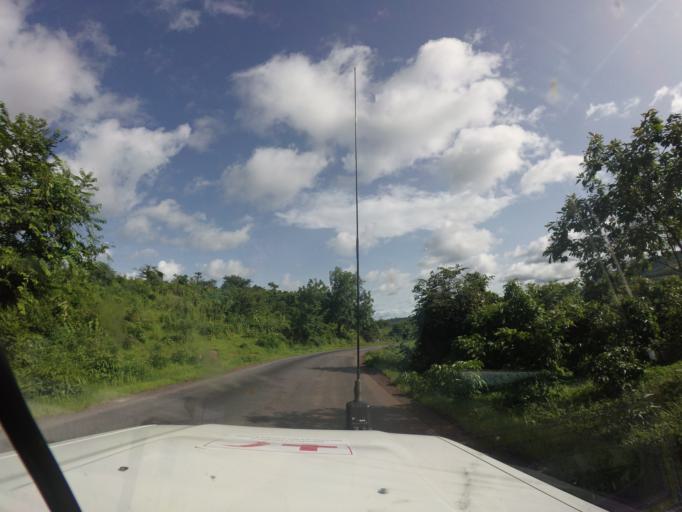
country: GN
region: Mamou
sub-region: Mamou Prefecture
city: Mamou
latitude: 10.2277
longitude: -12.4614
